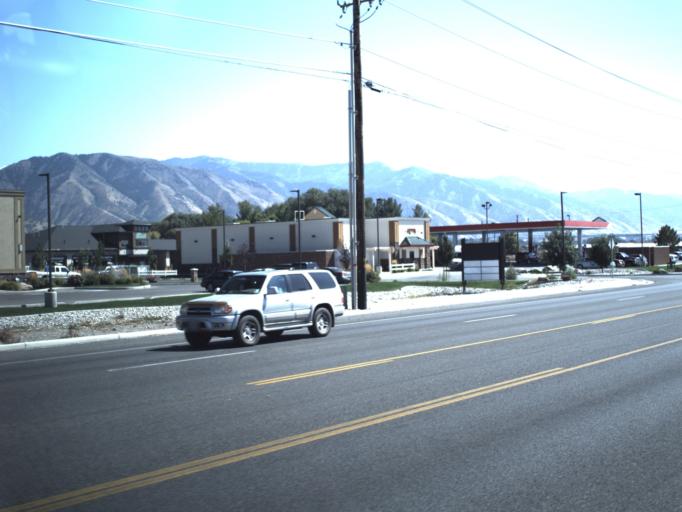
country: US
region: Utah
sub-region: Cache County
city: Hyde Park
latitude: 41.8010
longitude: -111.8336
